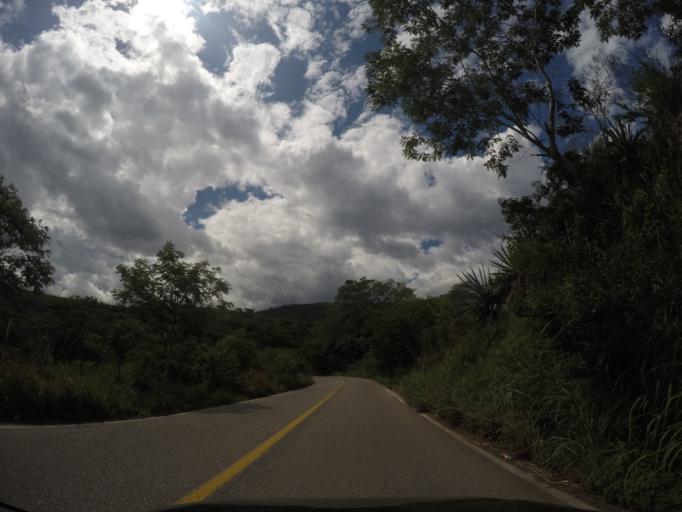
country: MX
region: Oaxaca
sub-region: San Jeronimo Coatlan
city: San Cristobal Honduras
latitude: 16.4316
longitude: -97.0671
